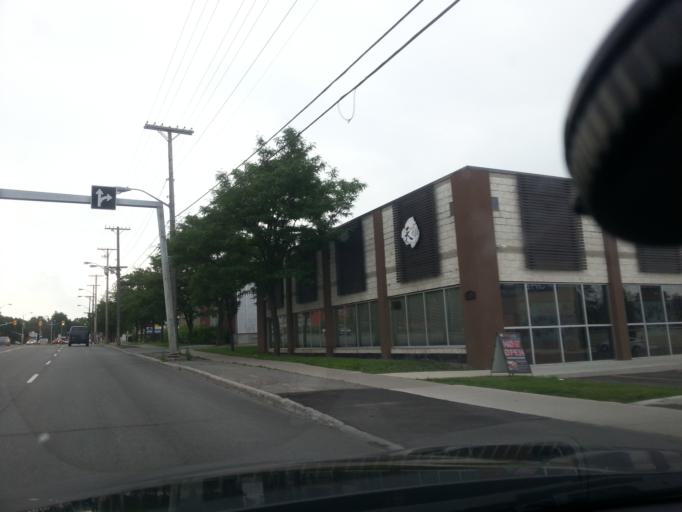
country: CA
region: Ontario
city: Ottawa
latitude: 45.3820
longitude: -75.6704
